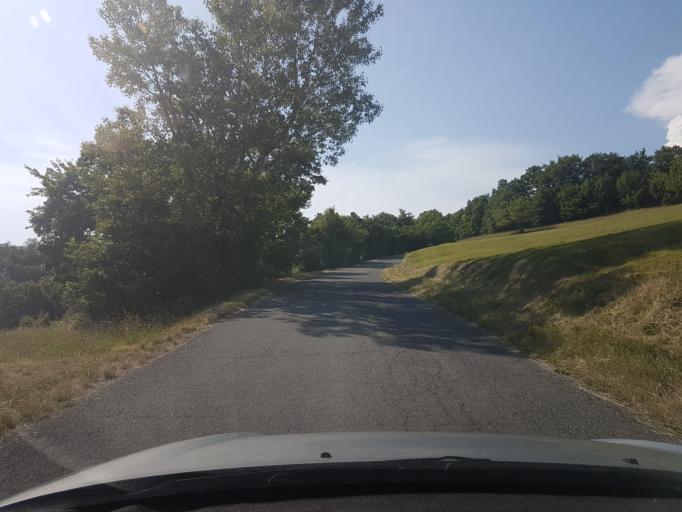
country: SI
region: Divaca
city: Divaca
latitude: 45.7624
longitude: 13.9826
